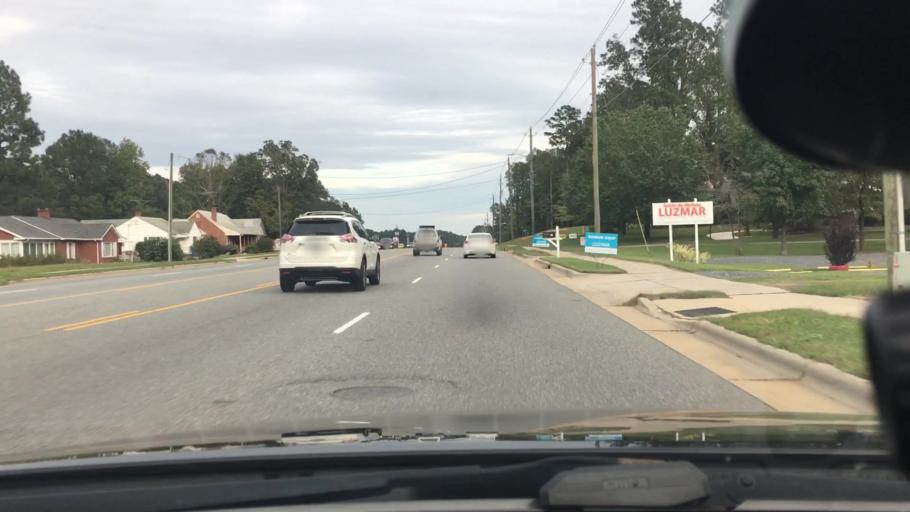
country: US
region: North Carolina
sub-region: Montgomery County
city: Biscoe
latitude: 35.3600
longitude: -79.7744
